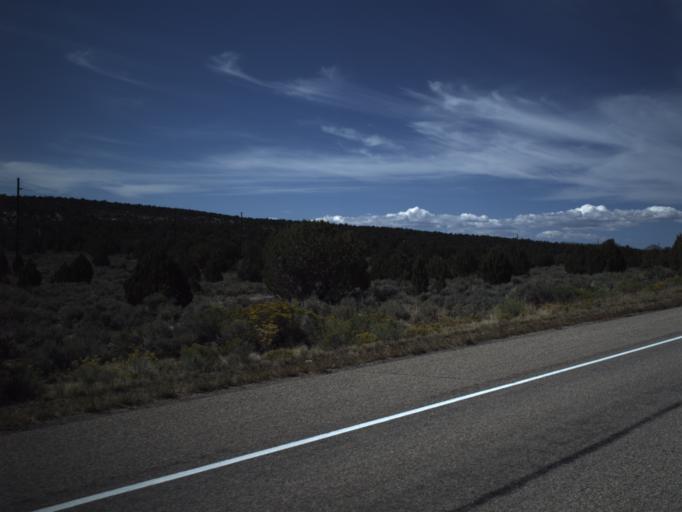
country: US
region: Utah
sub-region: Washington County
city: Ivins
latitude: 37.2721
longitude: -113.6425
